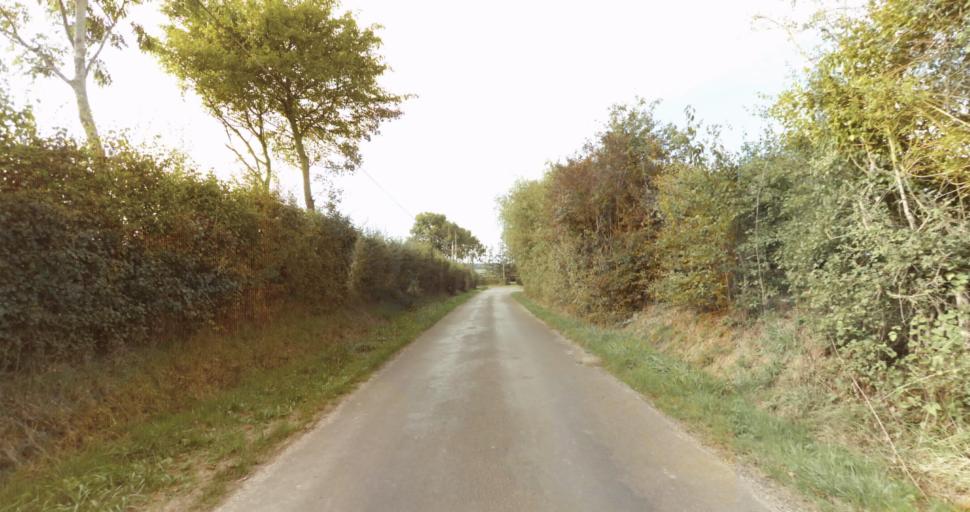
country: FR
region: Lower Normandy
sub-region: Departement de l'Orne
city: Gace
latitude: 48.7065
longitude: 0.2786
